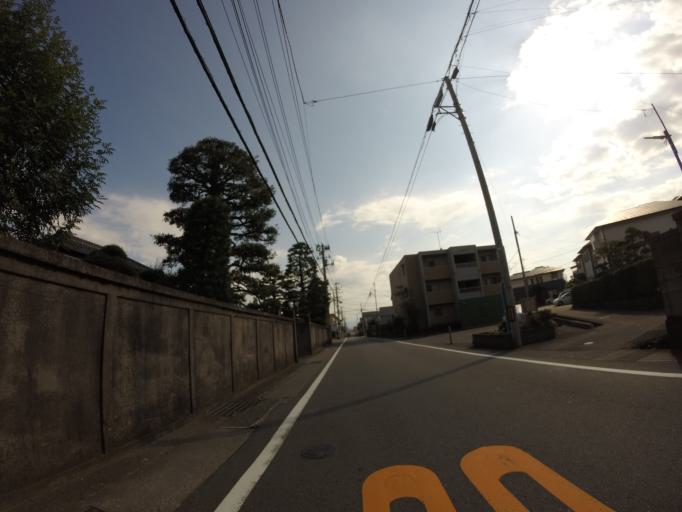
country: JP
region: Shizuoka
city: Fujinomiya
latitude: 35.1923
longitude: 138.6434
